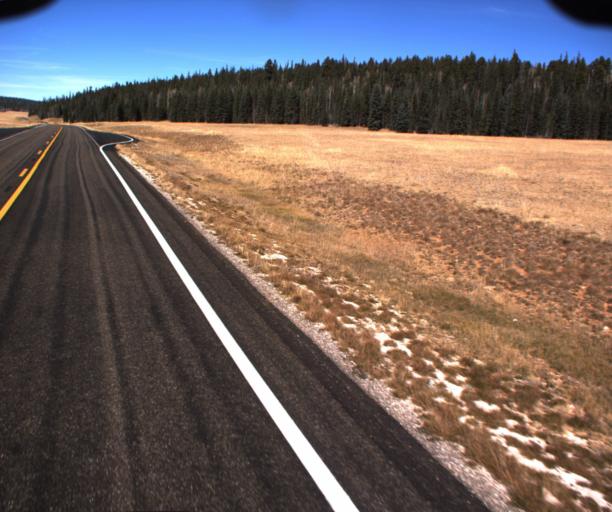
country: US
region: Arizona
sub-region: Coconino County
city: Grand Canyon
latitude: 36.3664
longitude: -112.1208
